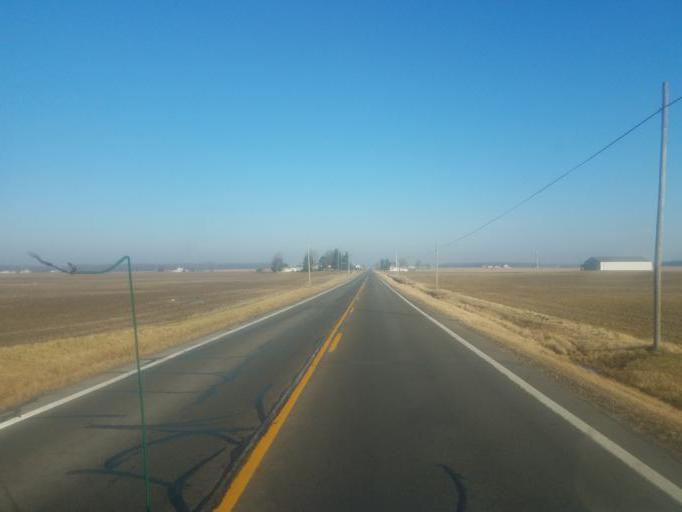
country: US
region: Ohio
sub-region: Crawford County
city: Bucyrus
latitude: 40.9094
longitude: -82.9544
